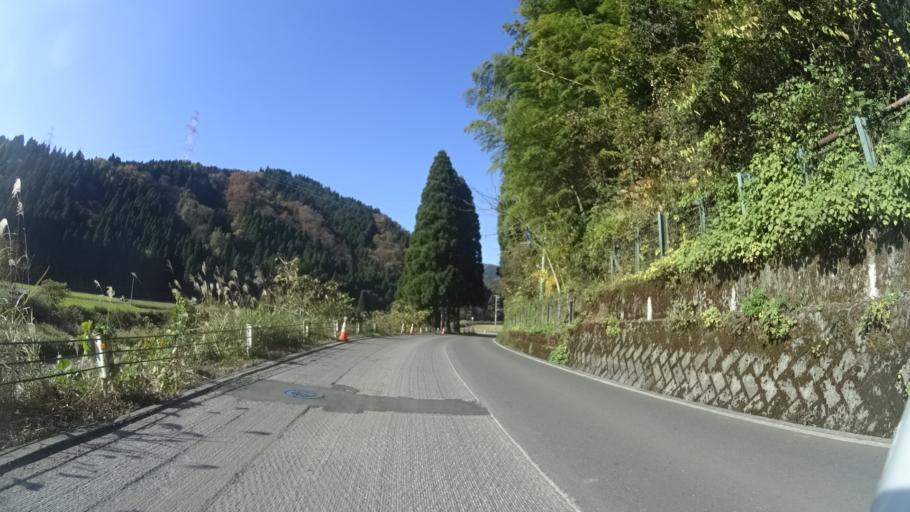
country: JP
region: Fukui
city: Ono
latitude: 35.9107
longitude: 136.3561
